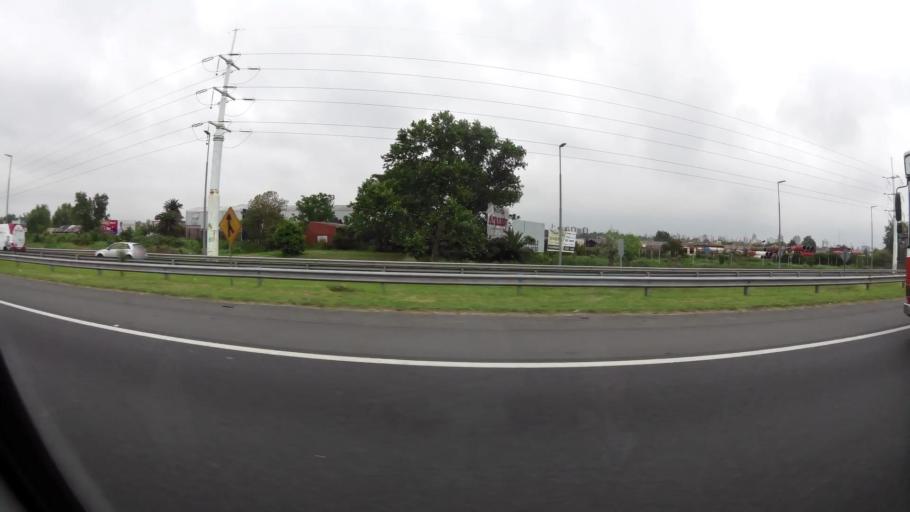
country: AR
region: Buenos Aires
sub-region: Partido de Quilmes
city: Quilmes
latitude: -34.7197
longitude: -58.2312
